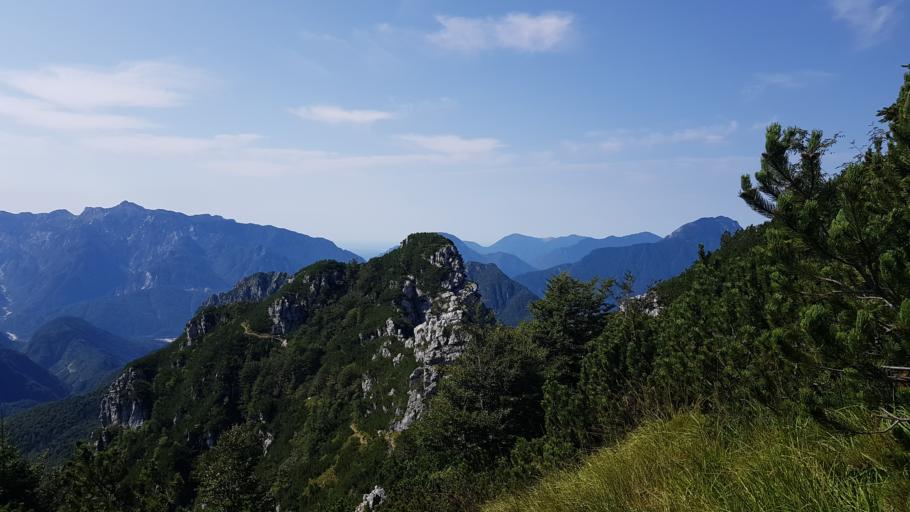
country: IT
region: Friuli Venezia Giulia
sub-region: Provincia di Udine
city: Moggio Udinese
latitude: 46.4707
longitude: 13.2192
